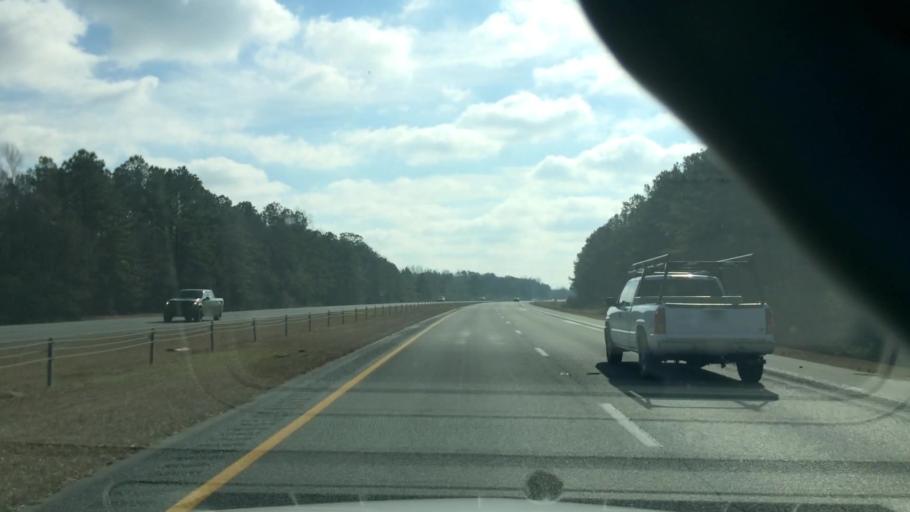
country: US
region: North Carolina
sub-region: Duplin County
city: Wallace
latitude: 34.6996
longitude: -77.9449
